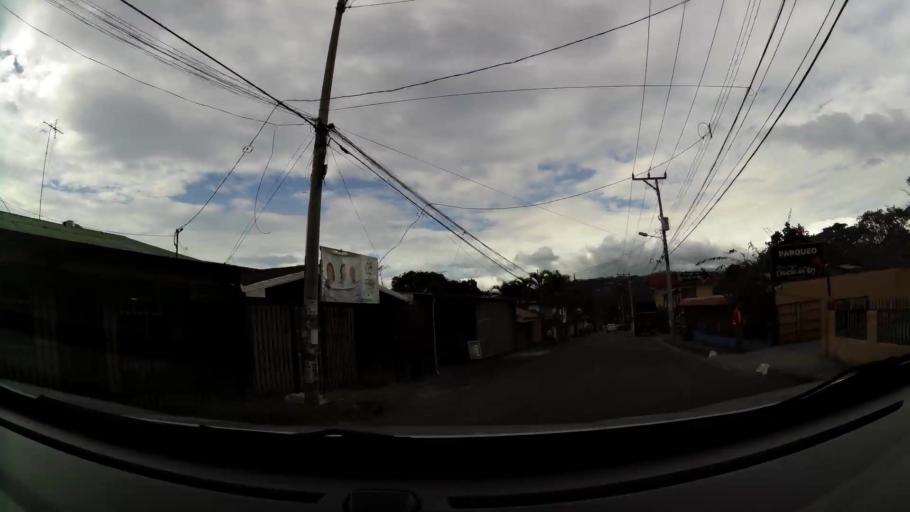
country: CR
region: San Jose
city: Santa Ana
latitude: 9.9310
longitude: -84.1786
